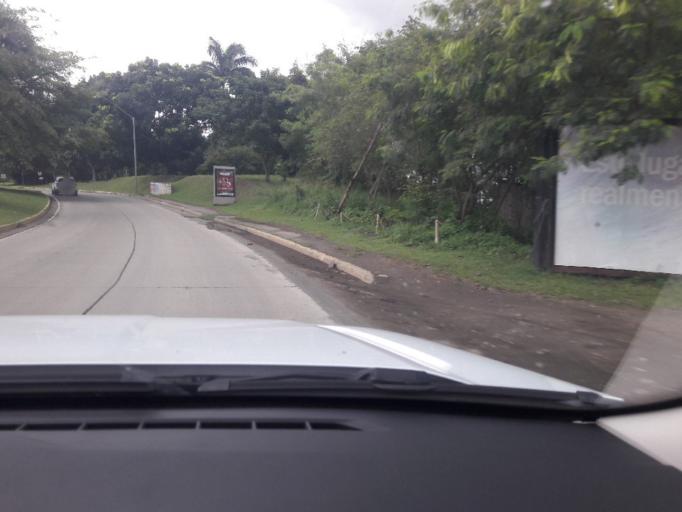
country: PA
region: Panama
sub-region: Distrito de Panama
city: Ancon
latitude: 8.9389
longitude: -79.5449
